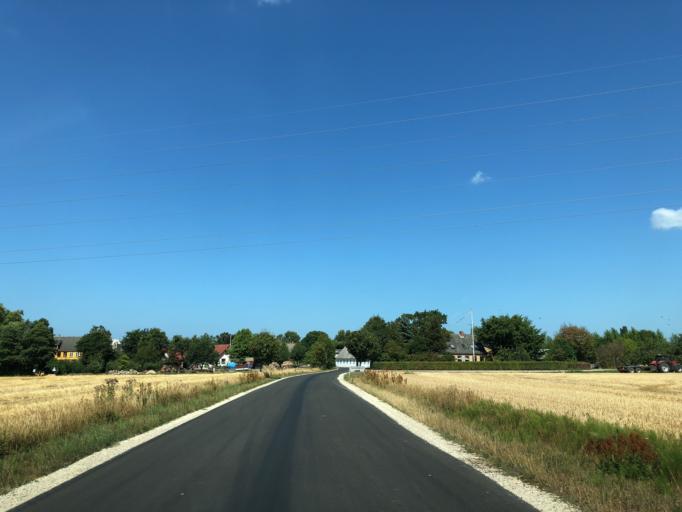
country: DK
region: Capital Region
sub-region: Halsnaes Kommune
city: Liseleje
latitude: 55.9733
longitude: 11.9157
